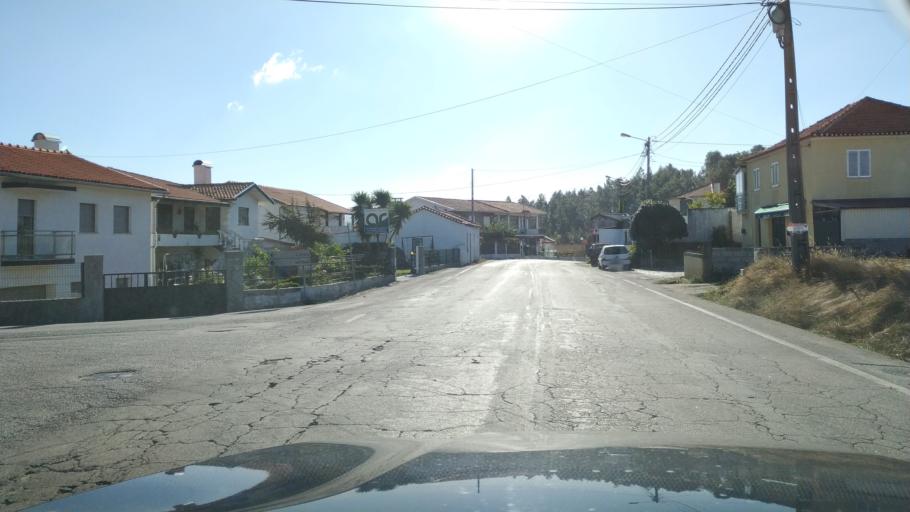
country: PT
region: Aveiro
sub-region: Vale de Cambra
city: Vale de Cambra
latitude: 40.8736
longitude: -8.4153
